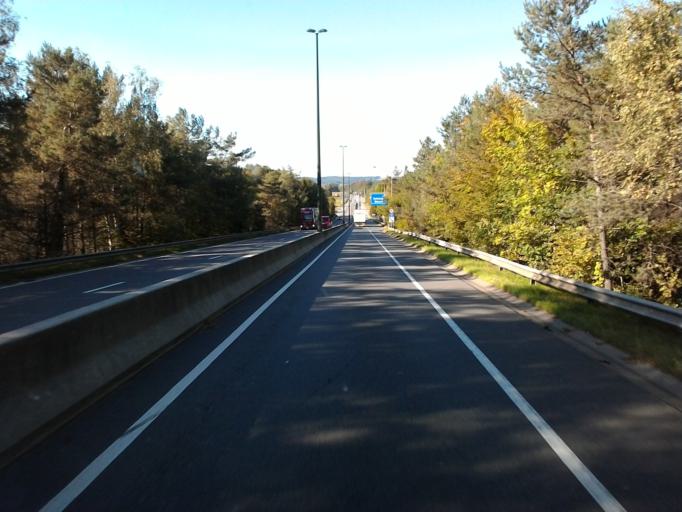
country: BE
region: Wallonia
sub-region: Province du Luxembourg
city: Attert
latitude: 49.7202
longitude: 5.7998
